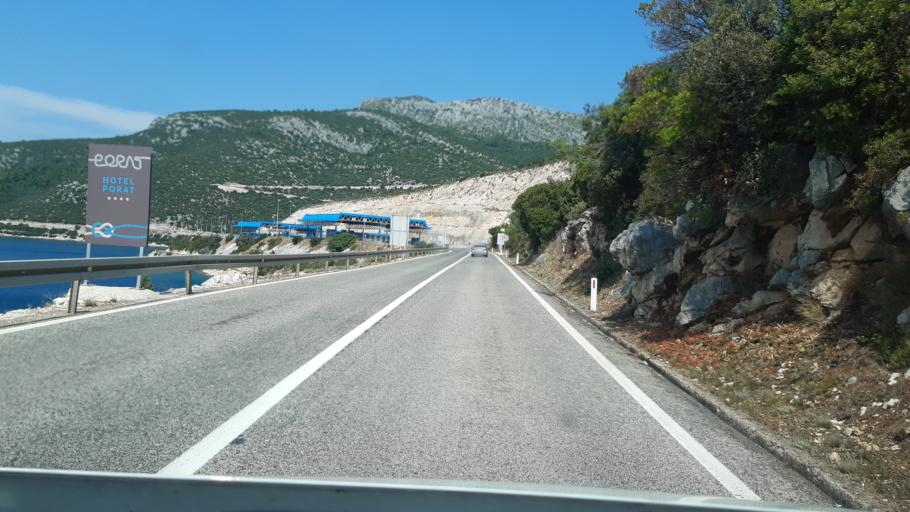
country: BA
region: Federation of Bosnia and Herzegovina
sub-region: Hercegovacko-Bosanski Kanton
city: Neum
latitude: 42.9372
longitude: 17.5823
